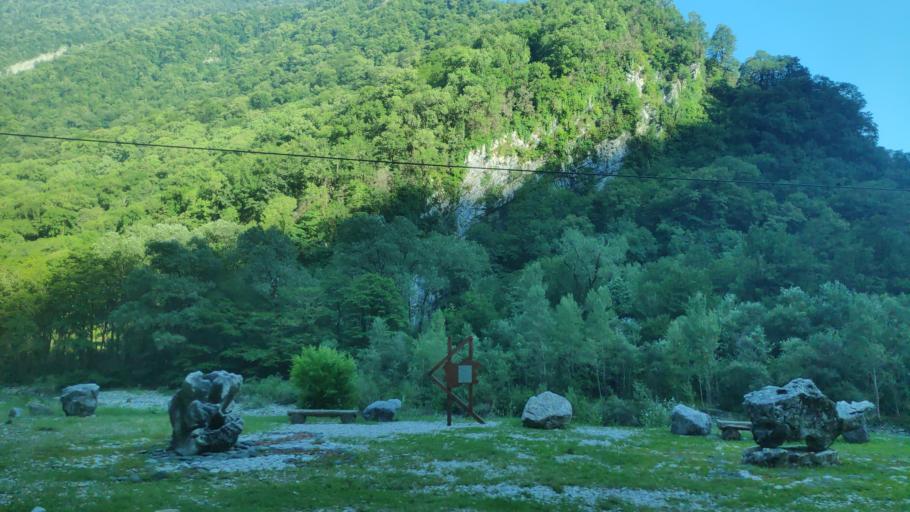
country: GE
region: Abkhazia
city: Gagra
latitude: 43.3523
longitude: 40.4144
